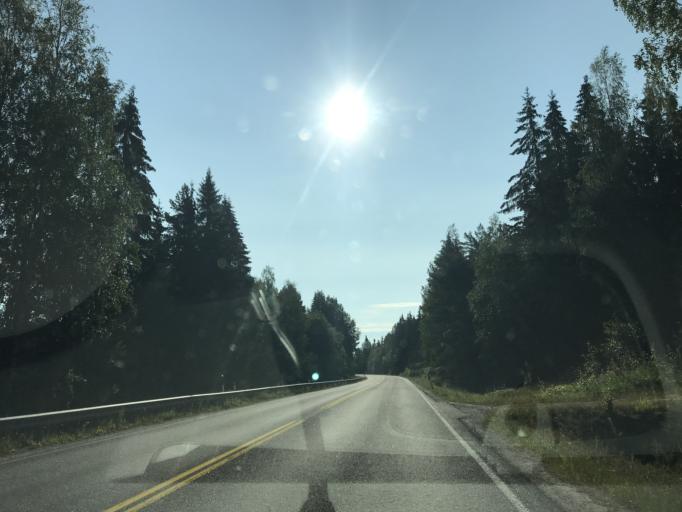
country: FI
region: Paijanne Tavastia
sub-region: Lahti
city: Orimattila
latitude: 60.7919
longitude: 25.6611
